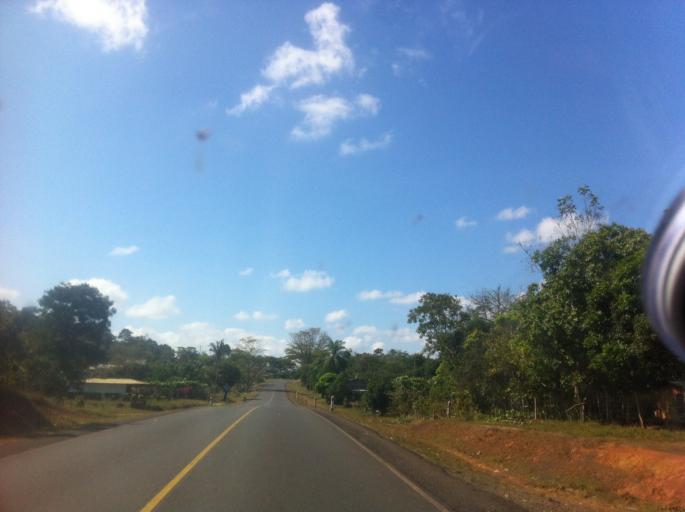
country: NI
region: Rio San Juan
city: San Carlos
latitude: 11.1721
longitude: -84.7430
